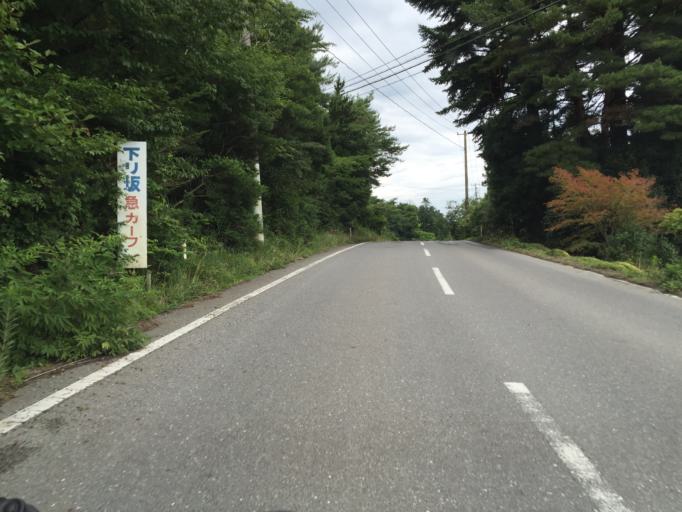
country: JP
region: Fukushima
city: Namie
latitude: 37.7461
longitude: 141.0012
